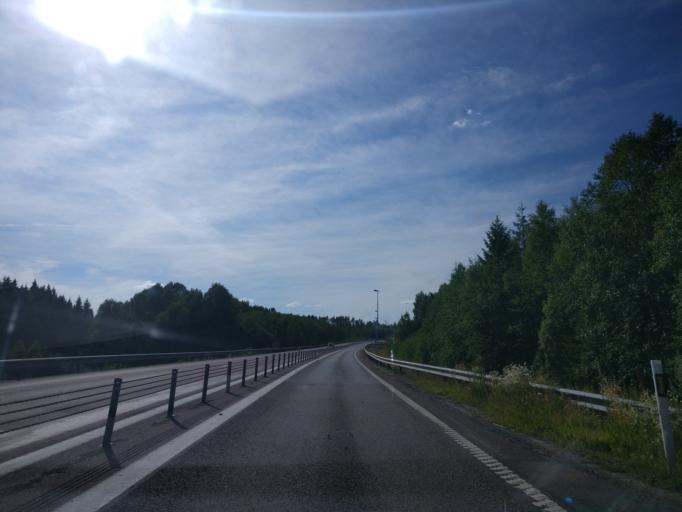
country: SE
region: Vaermland
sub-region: Karlstads Kommun
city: Edsvalla
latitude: 59.5097
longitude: 13.2206
